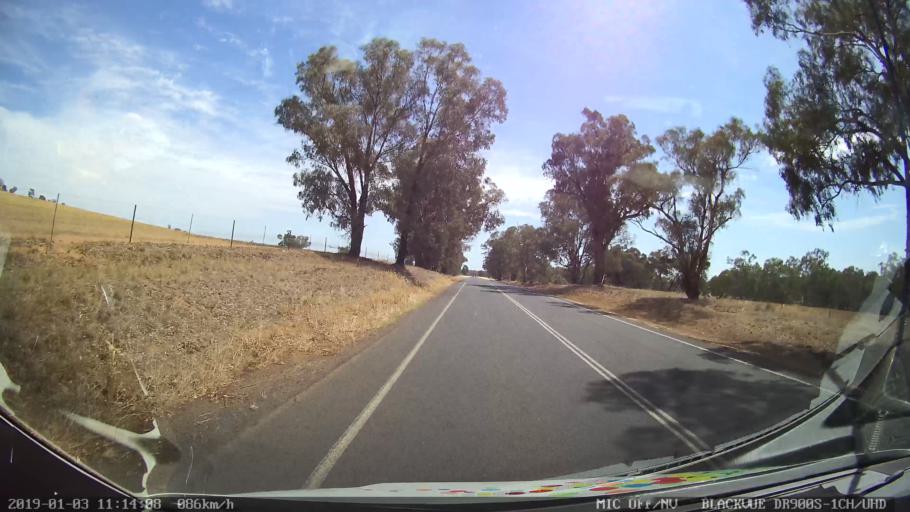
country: AU
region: New South Wales
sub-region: Young
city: Young
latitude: -34.1798
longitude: 148.2604
